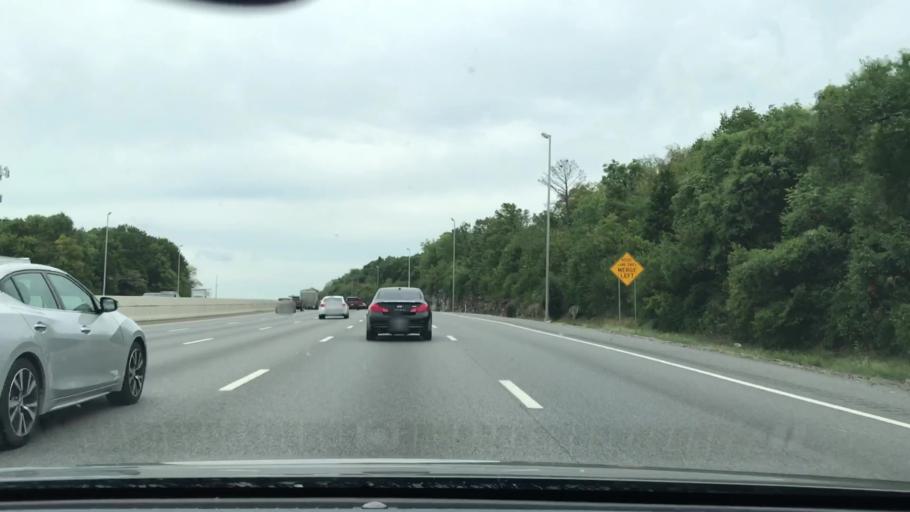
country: US
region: Tennessee
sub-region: Davidson County
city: Oak Hill
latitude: 36.1070
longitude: -86.7205
